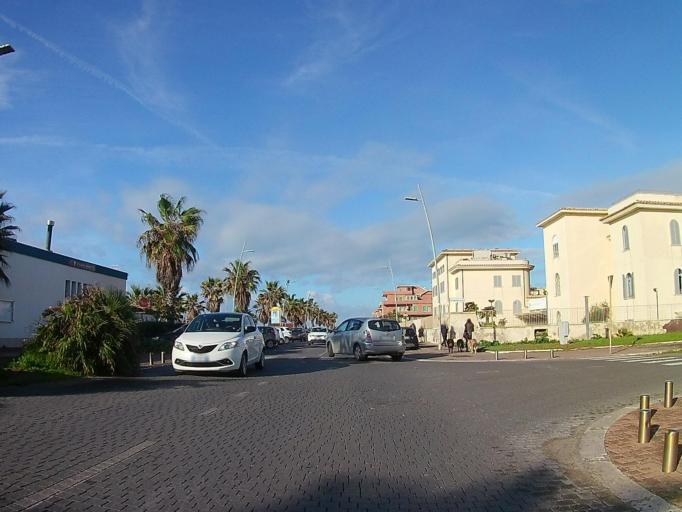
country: IT
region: Latium
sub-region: Citta metropolitana di Roma Capitale
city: Lido di Ostia
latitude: 41.7327
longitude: 12.2673
